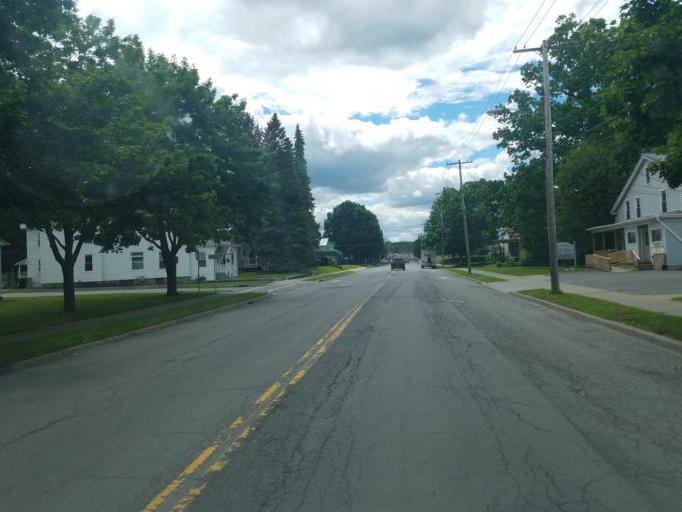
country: US
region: New York
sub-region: Herkimer County
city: Mohawk
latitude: 43.0126
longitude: -75.0000
